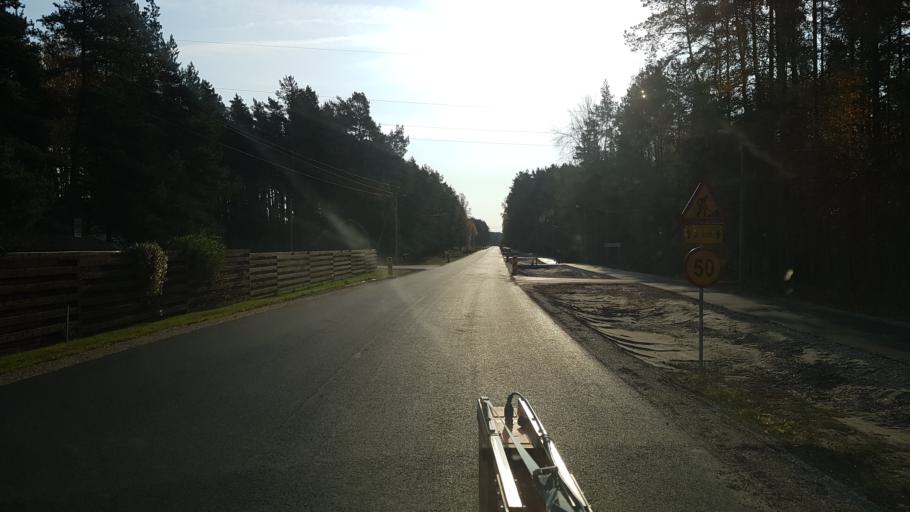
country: EE
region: Paernumaa
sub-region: Paikuse vald
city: Paikuse
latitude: 58.3617
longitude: 24.6074
